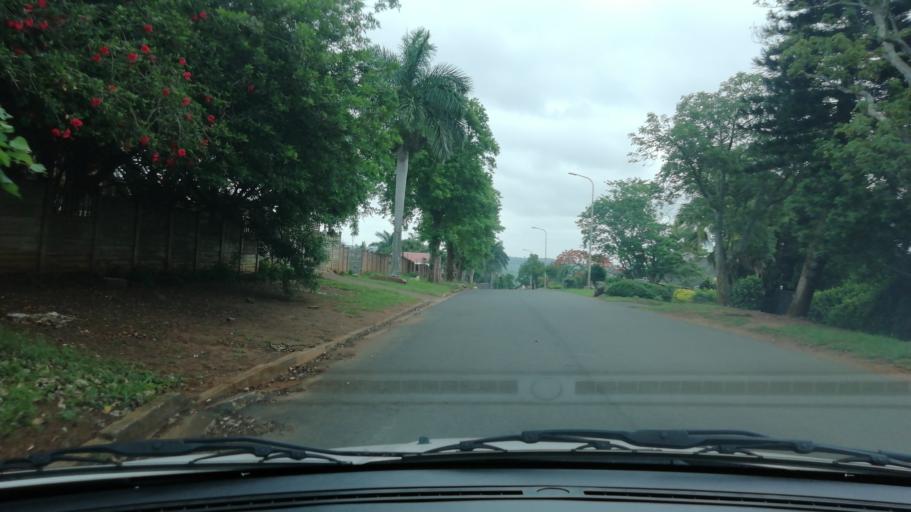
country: ZA
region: KwaZulu-Natal
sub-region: uThungulu District Municipality
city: Empangeni
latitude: -28.7659
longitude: 31.8900
